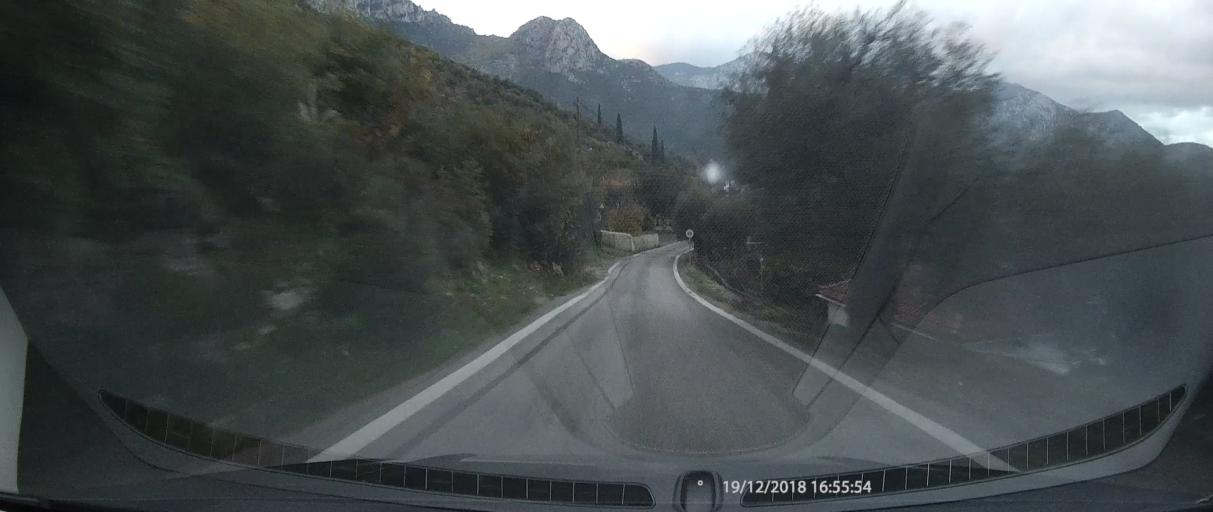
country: GR
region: Peloponnese
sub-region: Nomos Lakonias
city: Sykea
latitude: 36.9587
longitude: 22.9897
